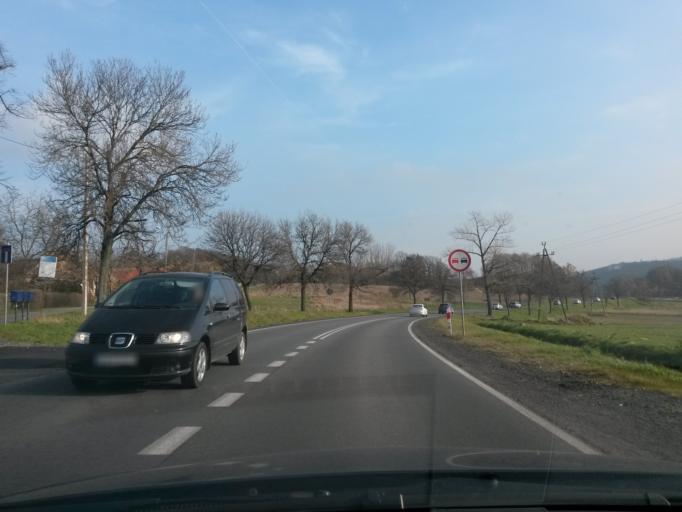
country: PL
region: Lower Silesian Voivodeship
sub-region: Powiat walbrzyski
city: Stare Bogaczowice
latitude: 50.9106
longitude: 16.2191
